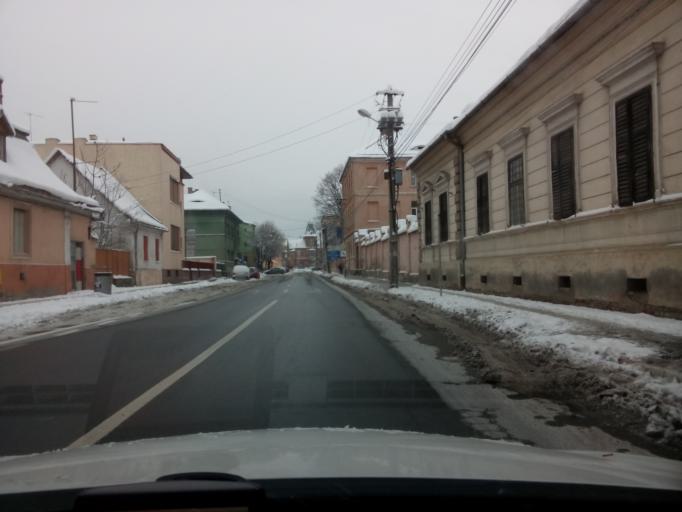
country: RO
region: Sibiu
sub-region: Municipiul Sibiu
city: Sibiu
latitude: 45.7936
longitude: 24.1444
